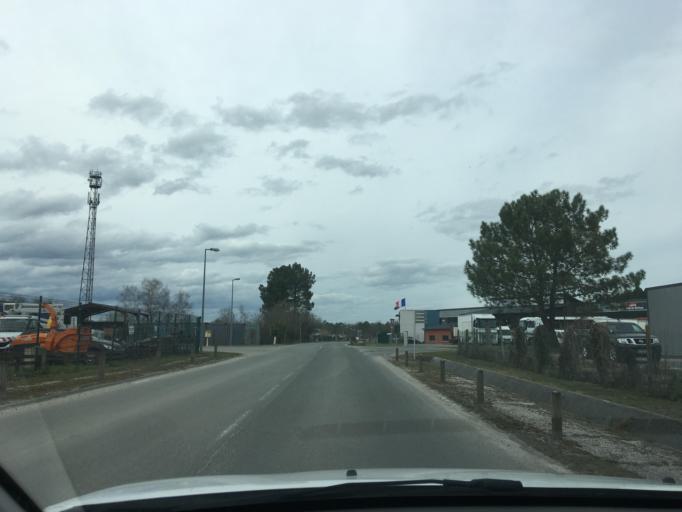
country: FR
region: Aquitaine
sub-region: Departement de la Gironde
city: Saint-Sauveur
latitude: 45.2205
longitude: -0.8723
